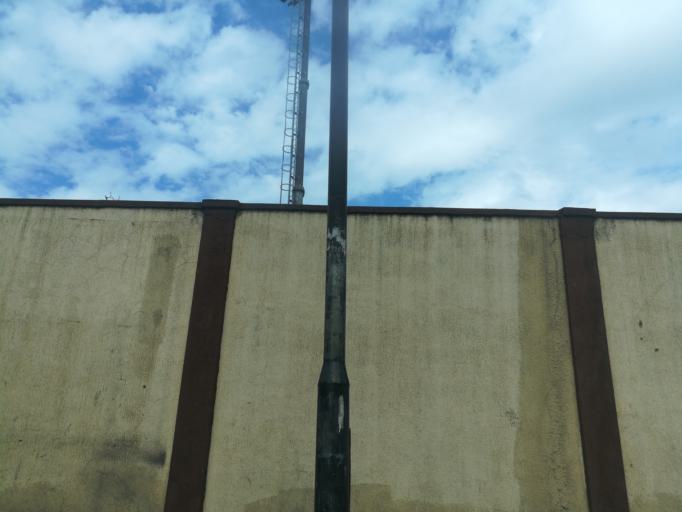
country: NG
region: Lagos
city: Agege
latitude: 6.6241
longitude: 3.3290
